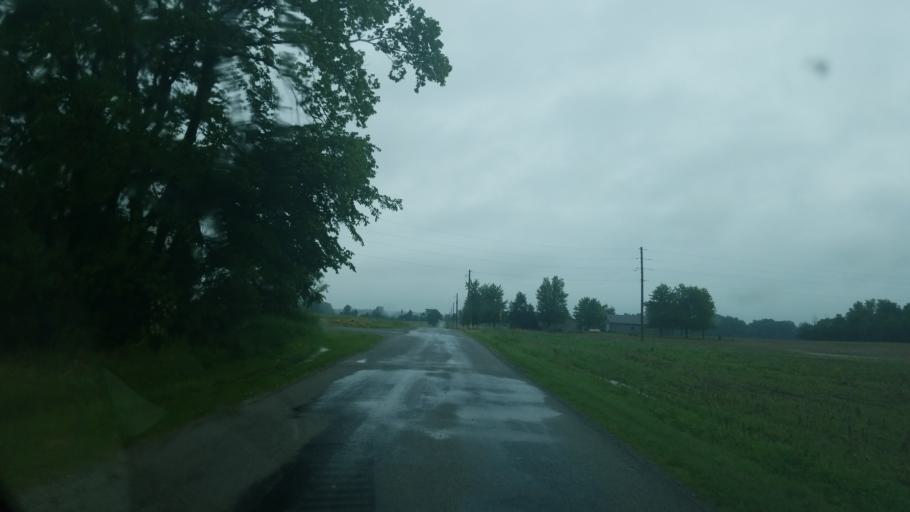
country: US
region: Ohio
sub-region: Huron County
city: Willard
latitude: 40.9450
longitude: -82.7973
